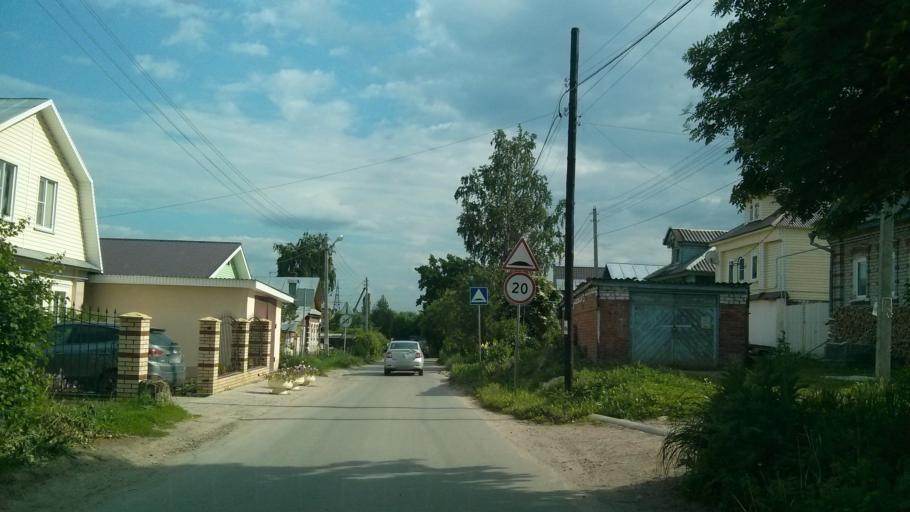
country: RU
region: Nizjnij Novgorod
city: Afonino
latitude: 56.2846
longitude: 44.1007
